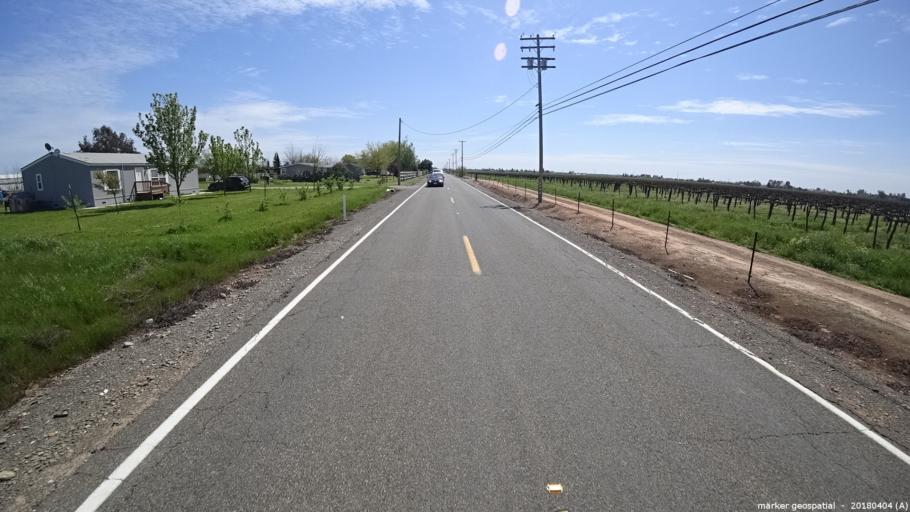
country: US
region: California
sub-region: Sacramento County
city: Herald
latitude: 38.3352
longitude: -121.2236
